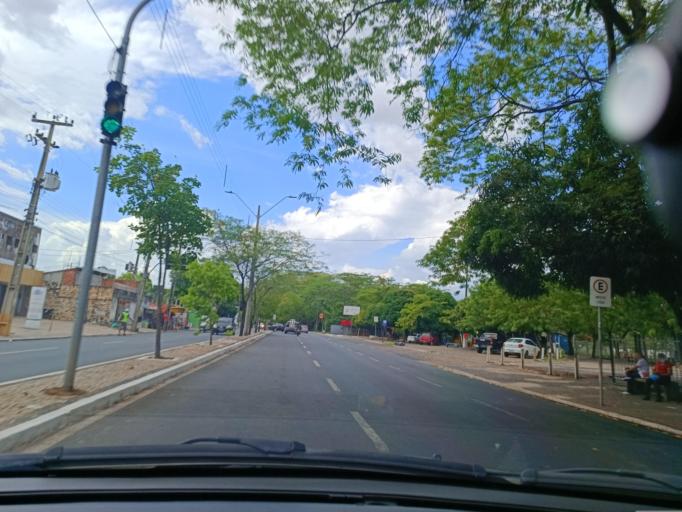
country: BR
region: Piaui
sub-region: Teresina
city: Teresina
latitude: -5.0849
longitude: -42.8040
